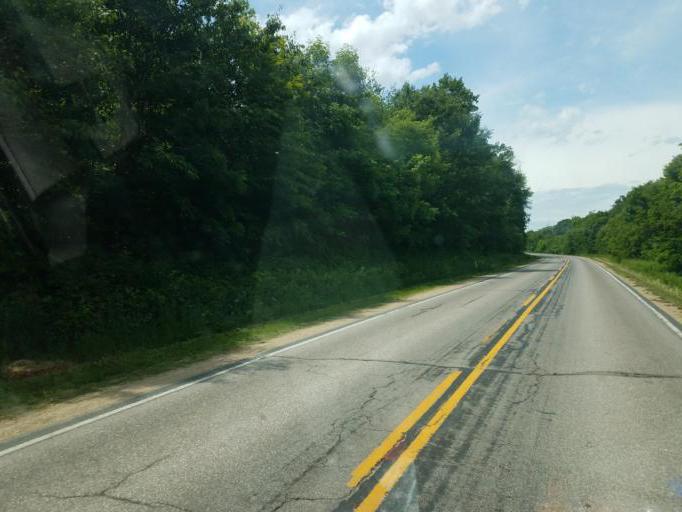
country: US
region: Wisconsin
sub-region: Vernon County
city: Hillsboro
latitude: 43.6367
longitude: -90.4464
